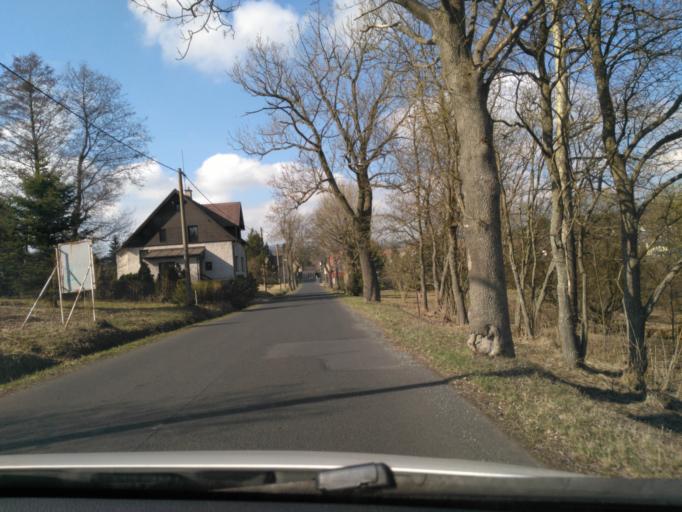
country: CZ
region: Ustecky
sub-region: Okres Chomutov
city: Kovarska
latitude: 50.4413
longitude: 13.0625
